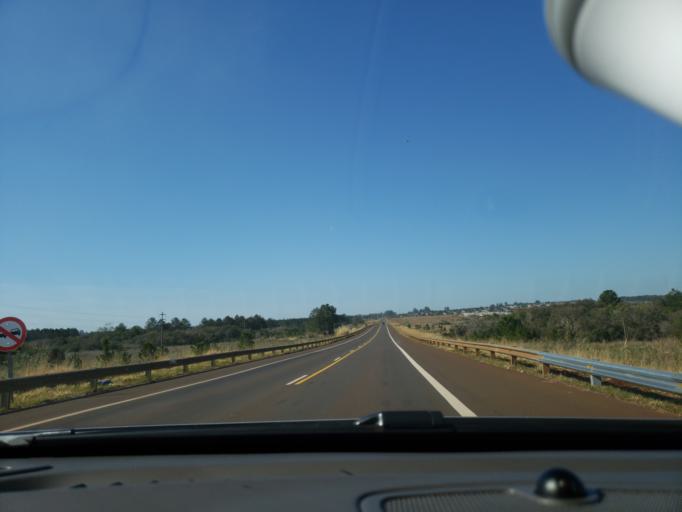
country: AR
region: Misiones
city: Garupa
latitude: -27.4647
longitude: -55.8979
